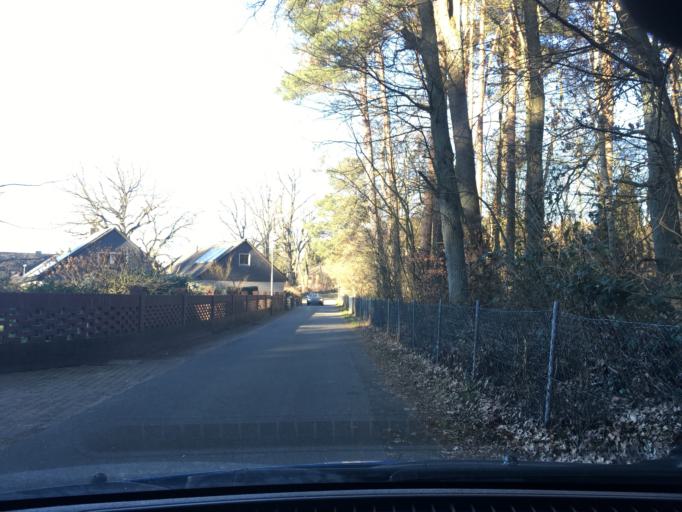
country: DE
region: Schleswig-Holstein
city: Schnakenbek
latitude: 53.3821
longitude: 10.5047
